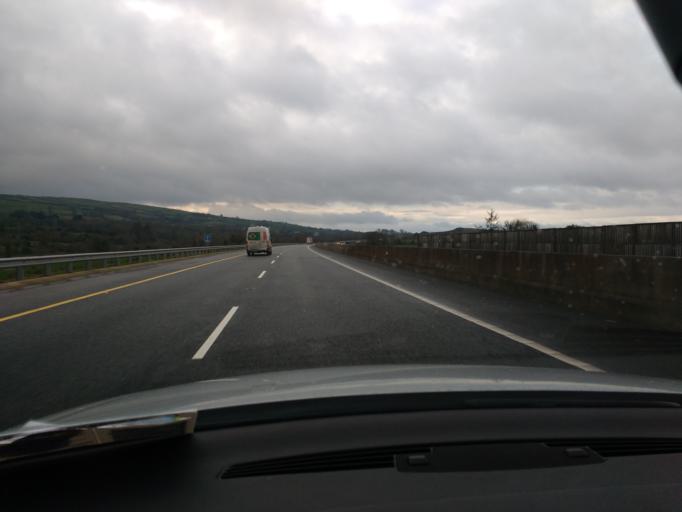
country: IE
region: Munster
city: Ballina
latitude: 52.7958
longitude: -8.3289
